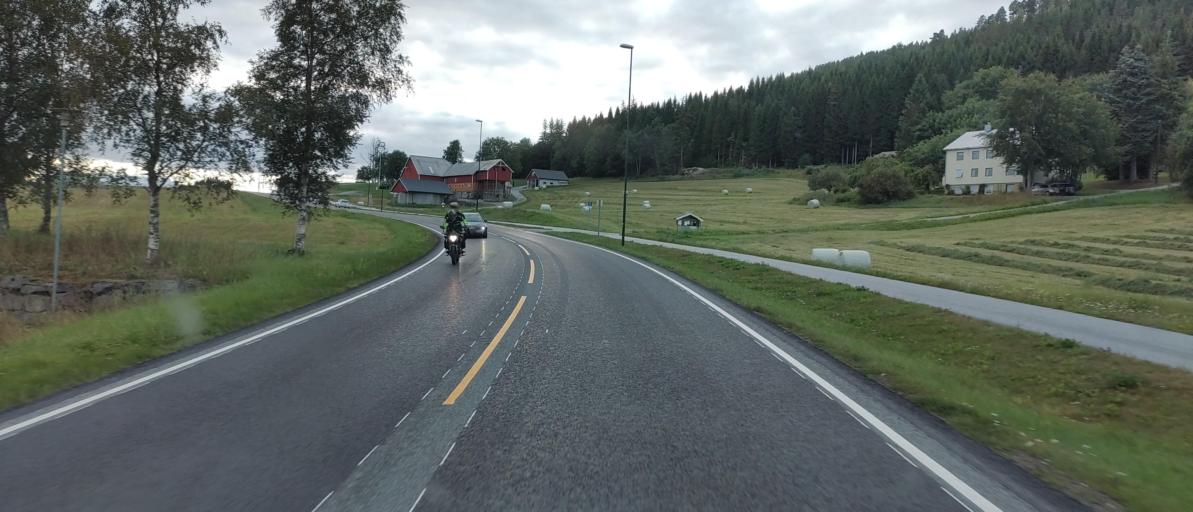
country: NO
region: More og Romsdal
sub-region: Molde
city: Hjelset
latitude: 62.7335
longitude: 7.4189
